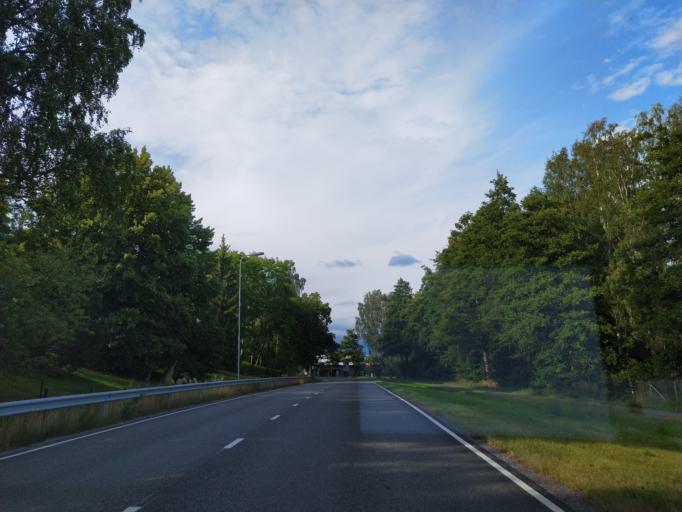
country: FI
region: Varsinais-Suomi
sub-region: Turku
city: Turku
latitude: 60.4245
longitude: 22.2269
